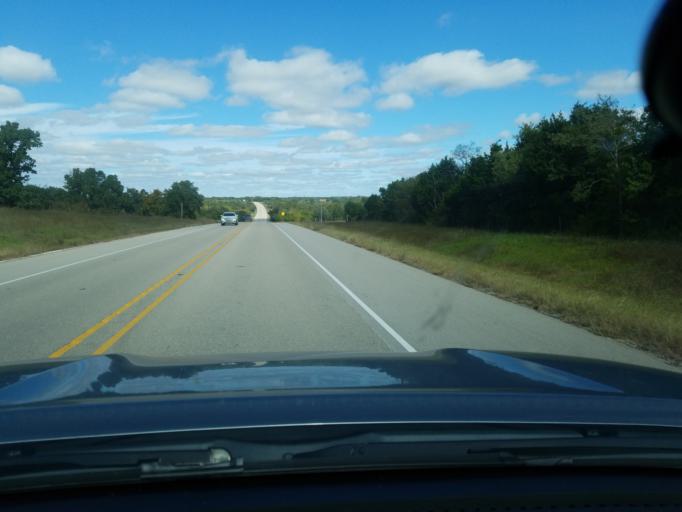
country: US
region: Texas
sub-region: Hamilton County
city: Hamilton
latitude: 31.5776
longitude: -98.1575
